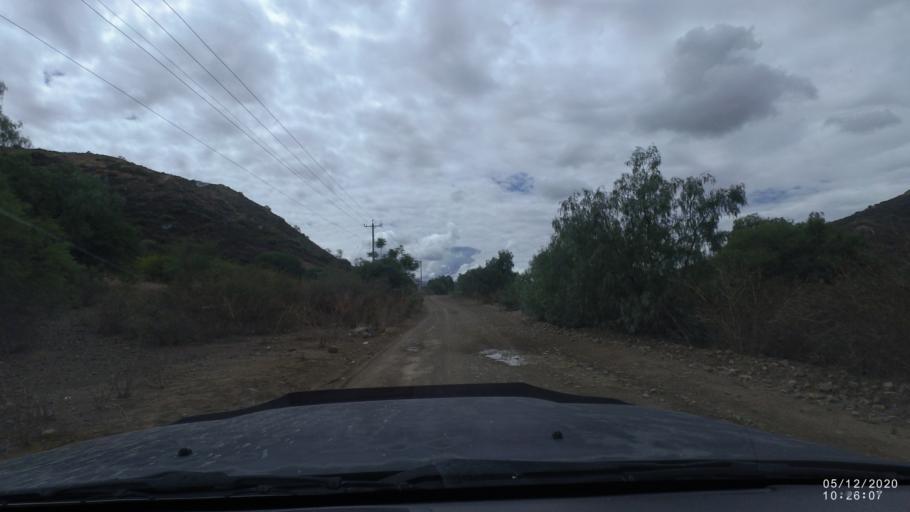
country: BO
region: Cochabamba
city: Sipe Sipe
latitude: -17.5239
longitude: -66.2847
